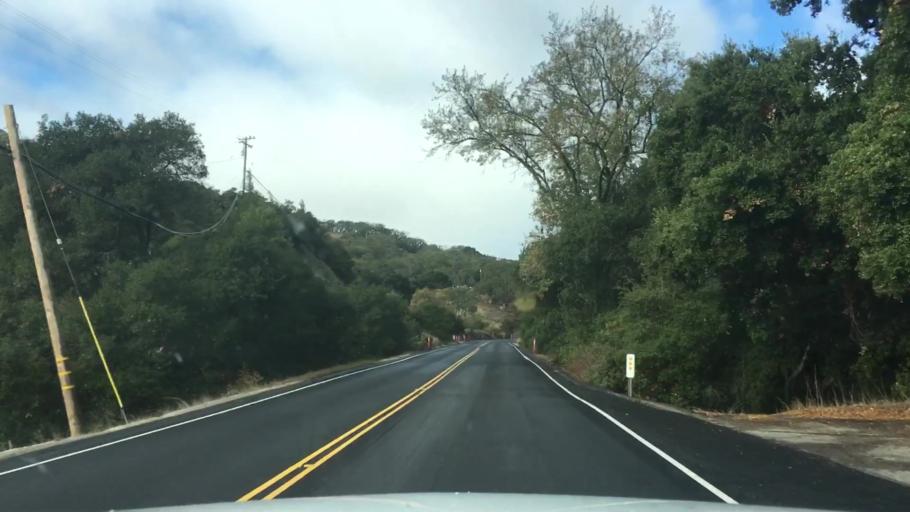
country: US
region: California
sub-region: San Luis Obispo County
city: Atascadero
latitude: 35.4513
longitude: -120.7056
